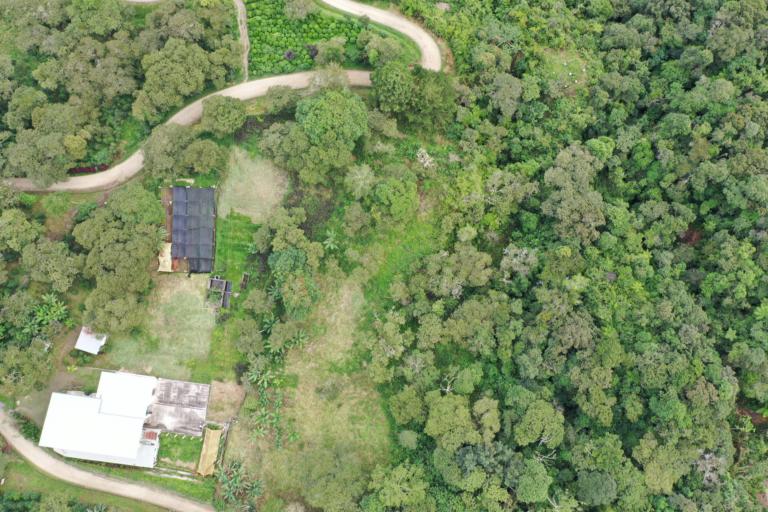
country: BO
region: La Paz
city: Coroico
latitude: -16.2599
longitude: -67.6940
